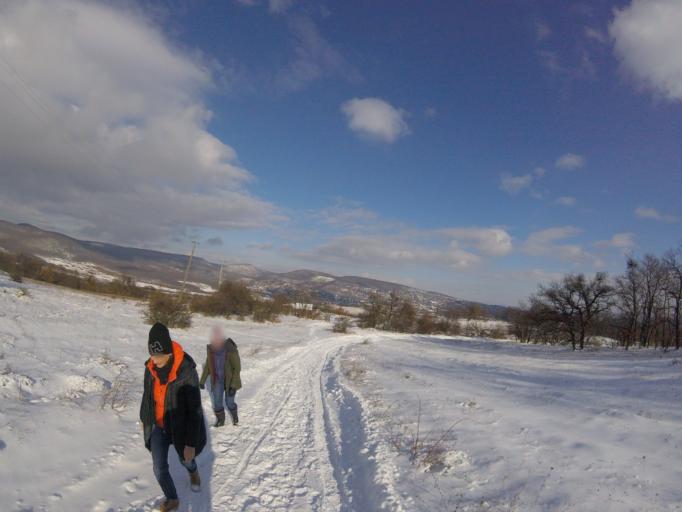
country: HU
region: Pest
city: Nagykovacsi
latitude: 47.6802
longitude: 19.0211
